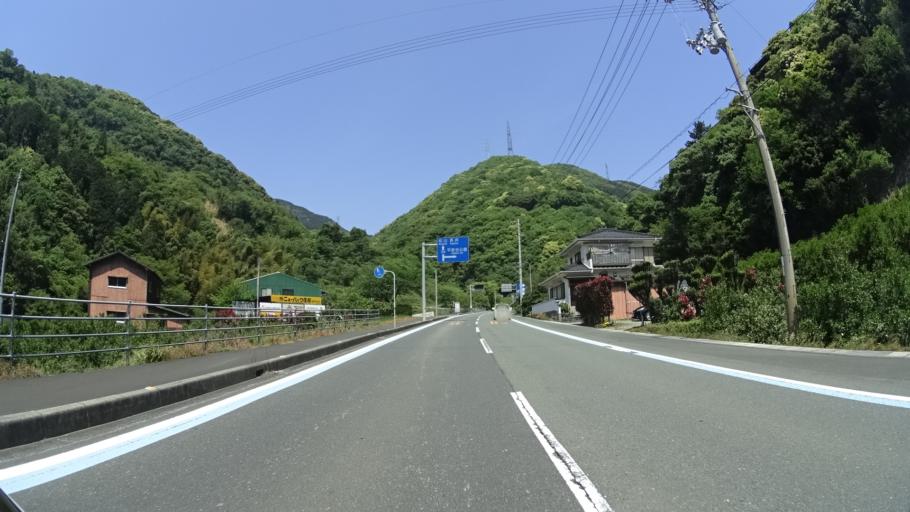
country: JP
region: Ehime
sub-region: Nishiuwa-gun
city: Ikata-cho
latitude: 33.5067
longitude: 132.3975
